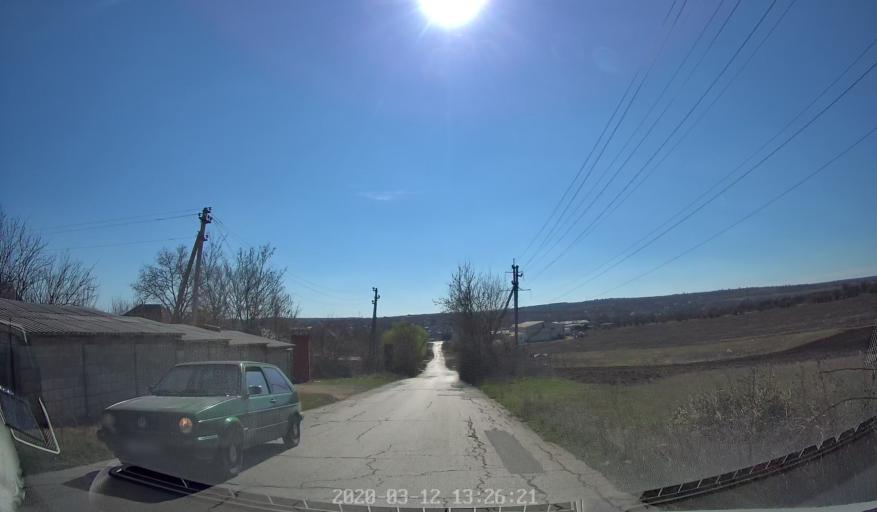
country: MD
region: Laloveni
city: Ialoveni
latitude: 46.9353
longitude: 28.8152
